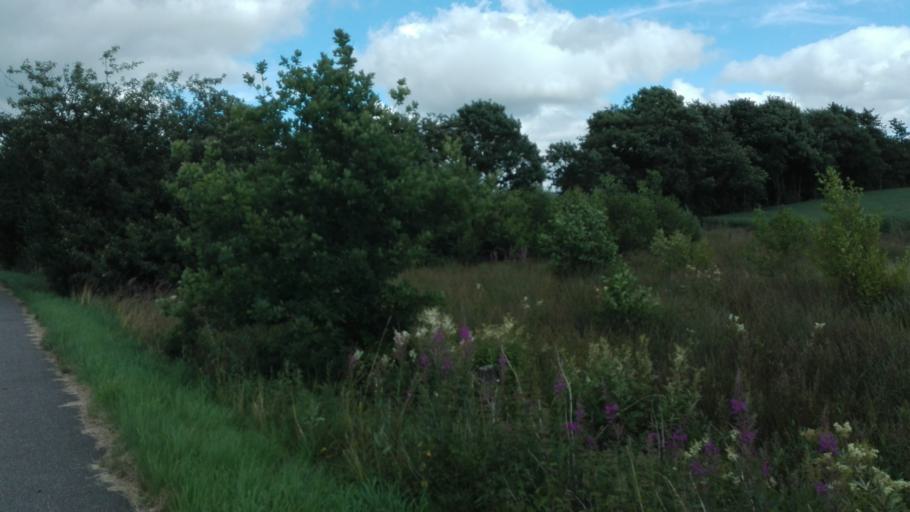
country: DK
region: Central Jutland
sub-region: Silkeborg Kommune
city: Virklund
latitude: 56.0671
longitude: 9.4972
